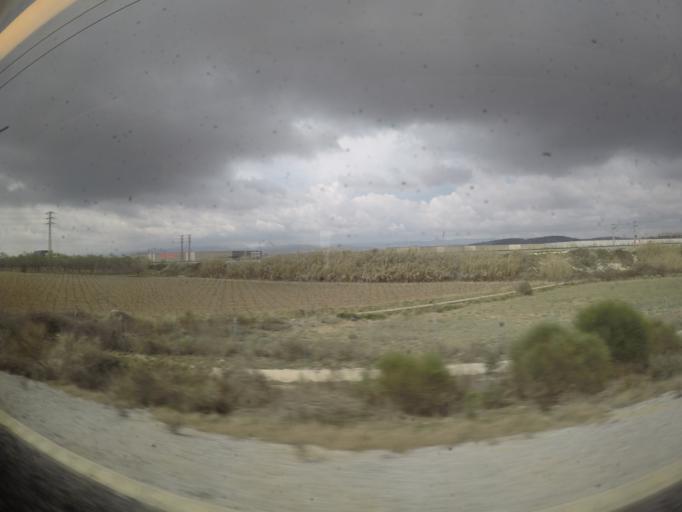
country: ES
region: Catalonia
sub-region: Provincia de Barcelona
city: Castellet
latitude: 41.3115
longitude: 1.6549
